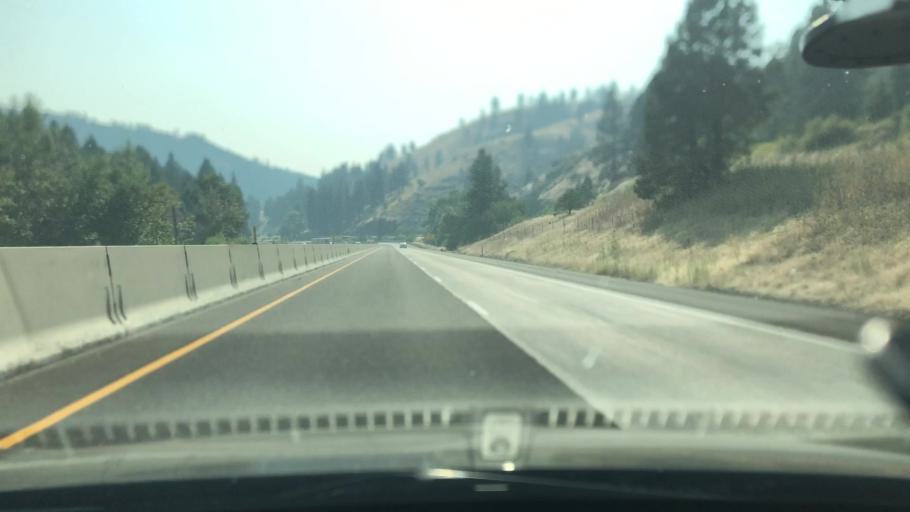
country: US
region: Oregon
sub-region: Union County
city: La Grande
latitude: 45.3542
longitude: -118.1914
